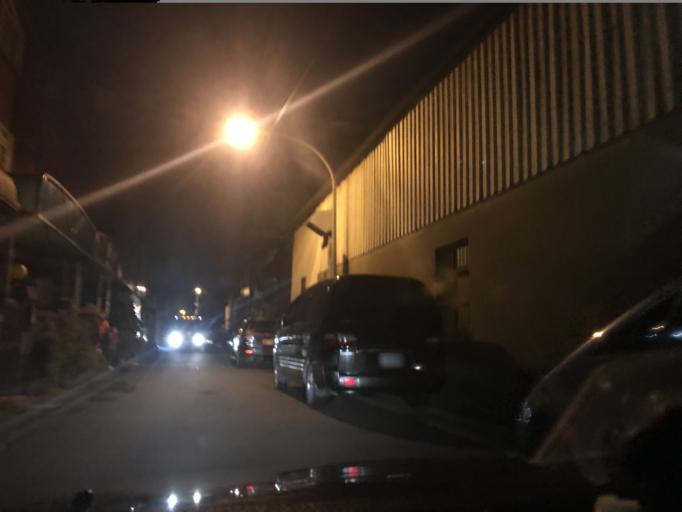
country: TW
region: Taiwan
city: Taoyuan City
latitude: 24.9763
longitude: 121.2333
